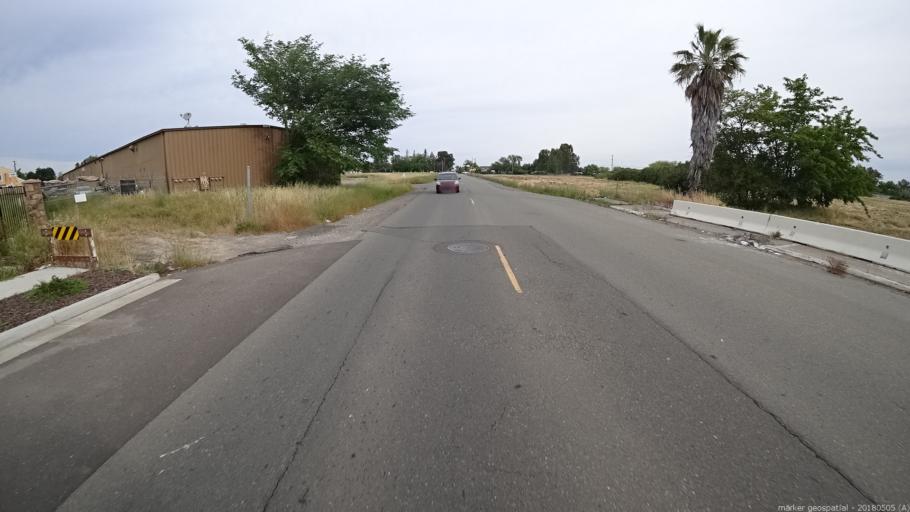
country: US
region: California
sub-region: Sacramento County
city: Rio Linda
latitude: 38.6494
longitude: -121.4366
